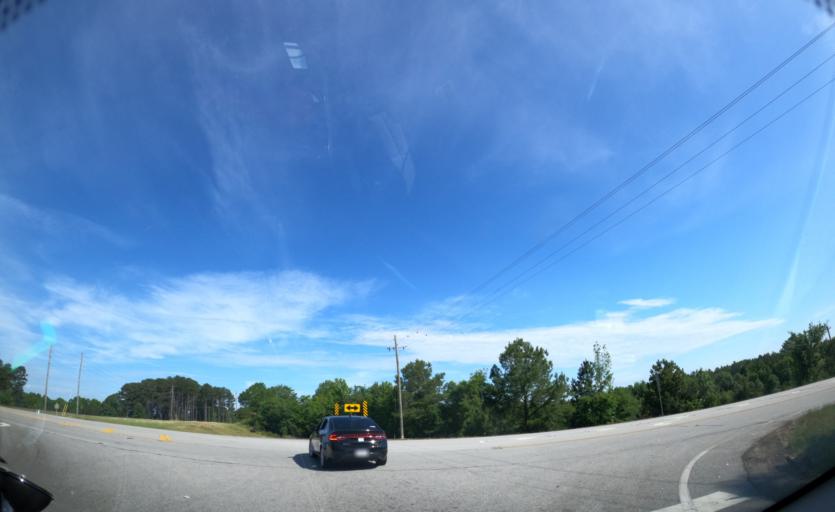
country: US
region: Georgia
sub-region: Lincoln County
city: Lincolnton
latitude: 33.8073
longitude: -82.4592
